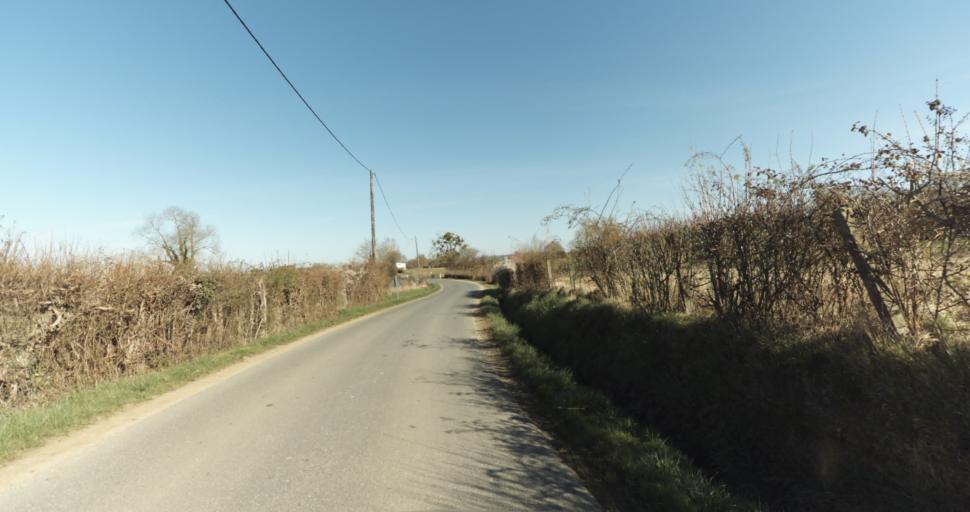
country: FR
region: Lower Normandy
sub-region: Departement de l'Orne
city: Trun
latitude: 48.9177
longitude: 0.0296
